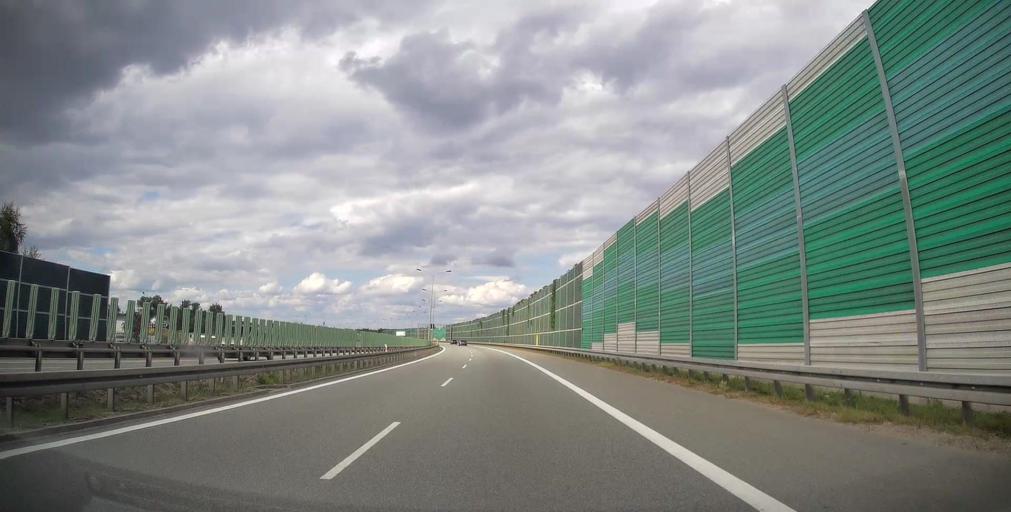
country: PL
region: Masovian Voivodeship
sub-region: Powiat bialobrzeski
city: Stara Blotnica
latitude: 51.5664
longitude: 21.0254
